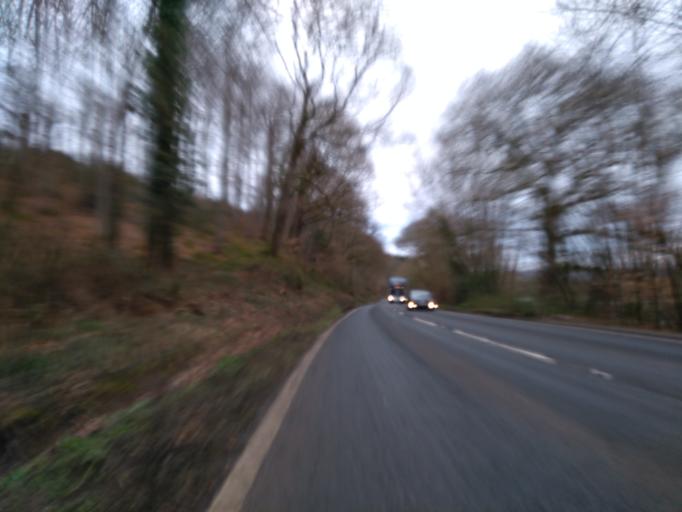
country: GB
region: England
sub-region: Devon
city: Exeter
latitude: 50.7566
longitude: -3.5218
